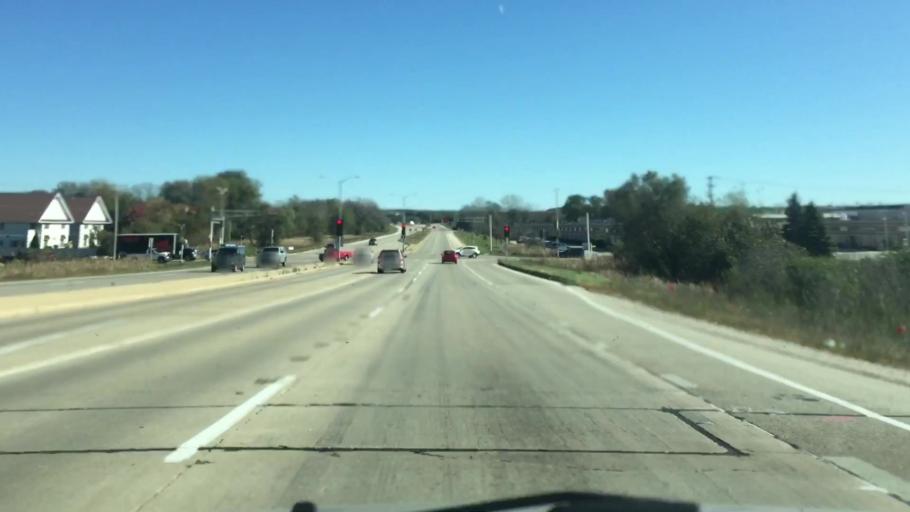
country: US
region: Wisconsin
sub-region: Waukesha County
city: Waukesha
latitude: 42.9770
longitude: -88.2373
